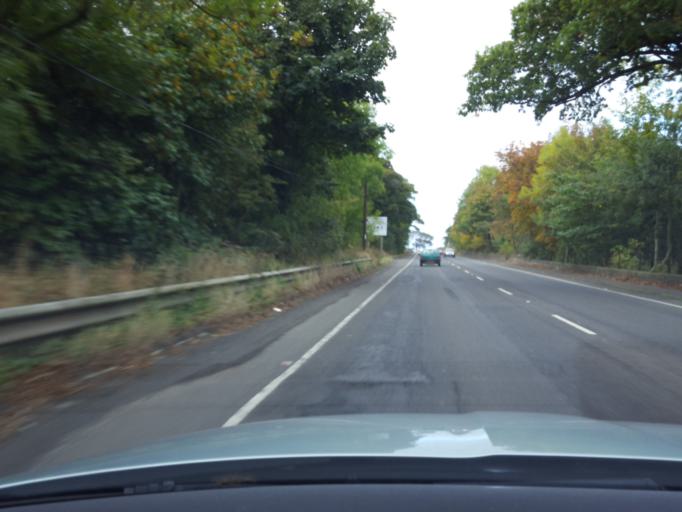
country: GB
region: Scotland
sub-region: Fife
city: Pathhead
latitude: 55.8870
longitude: -2.9936
